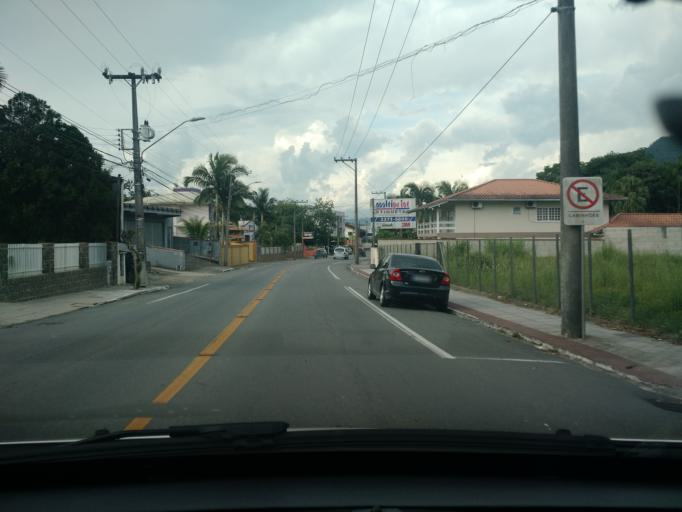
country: BR
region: Santa Catarina
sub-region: Jaragua Do Sul
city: Jaragua do Sul
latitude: -26.4878
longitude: -49.0921
